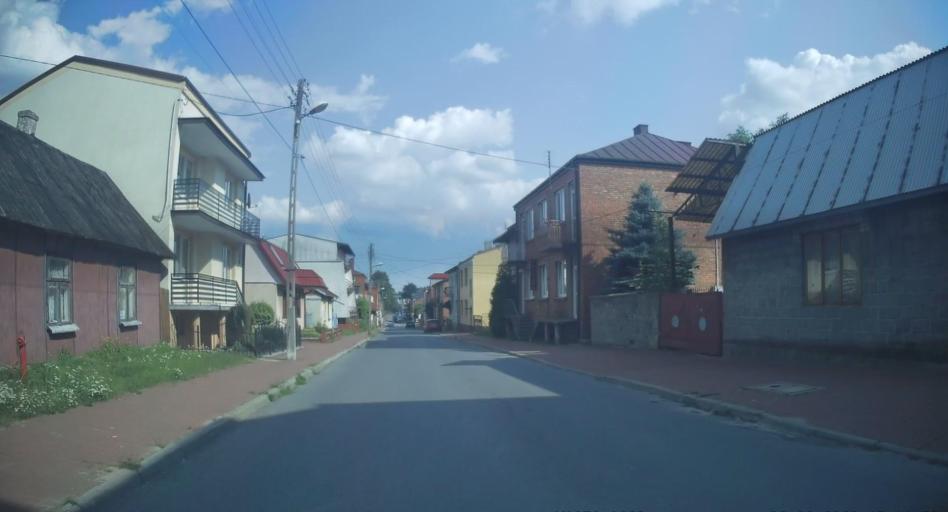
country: PL
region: Swietokrzyskie
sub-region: Powiat konecki
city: Radoszyce
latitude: 51.0747
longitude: 20.2569
